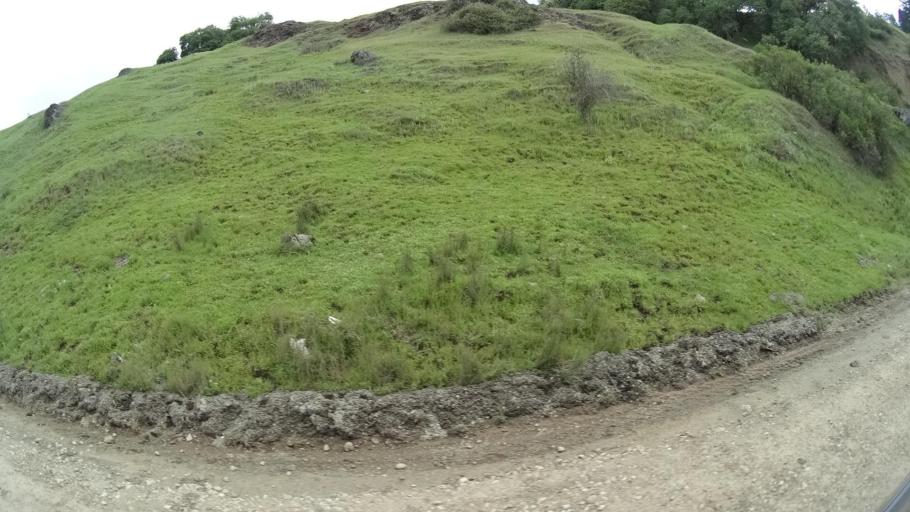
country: US
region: California
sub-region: Humboldt County
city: Redway
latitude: 40.1761
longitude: -123.5699
